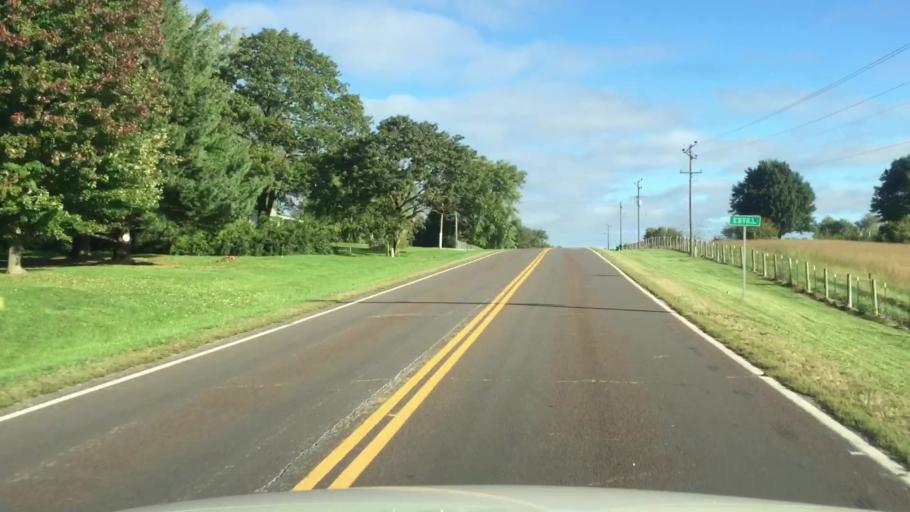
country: US
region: Missouri
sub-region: Howard County
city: New Franklin
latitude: 39.0447
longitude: -92.7444
